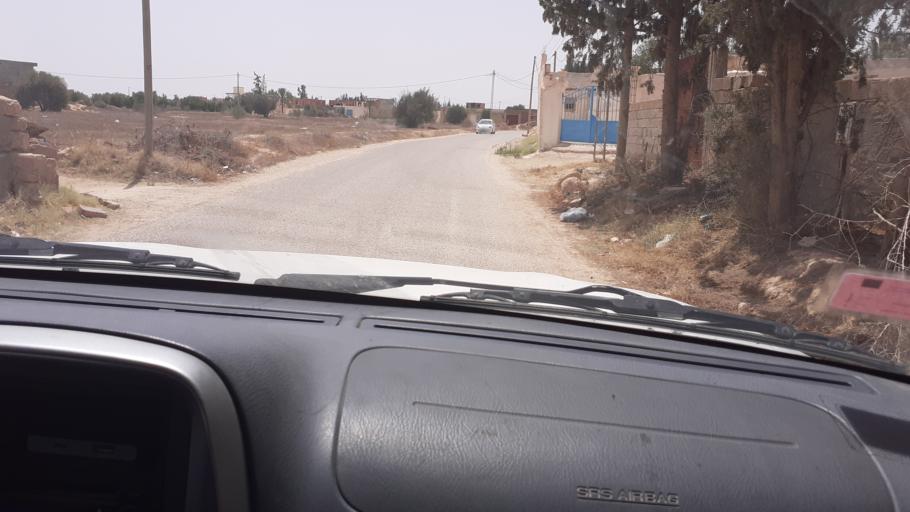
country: TN
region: Qabis
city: Matmata
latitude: 33.6124
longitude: 10.2873
